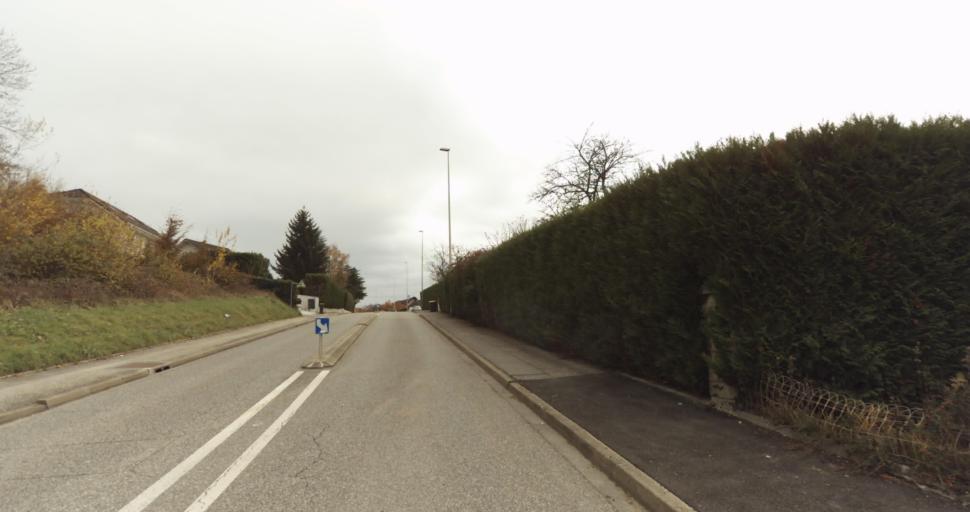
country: FR
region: Rhone-Alpes
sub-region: Departement de la Haute-Savoie
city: Annecy-le-Vieux
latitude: 45.9289
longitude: 6.1395
